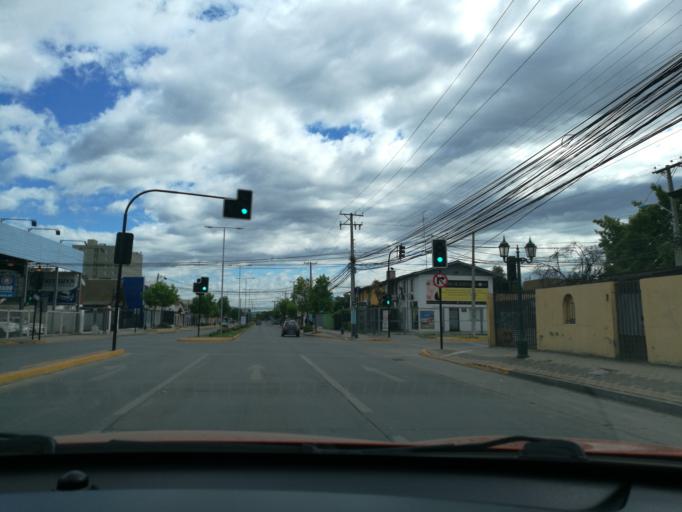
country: CL
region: O'Higgins
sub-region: Provincia de Cachapoal
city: Rancagua
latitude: -34.1693
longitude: -70.7348
